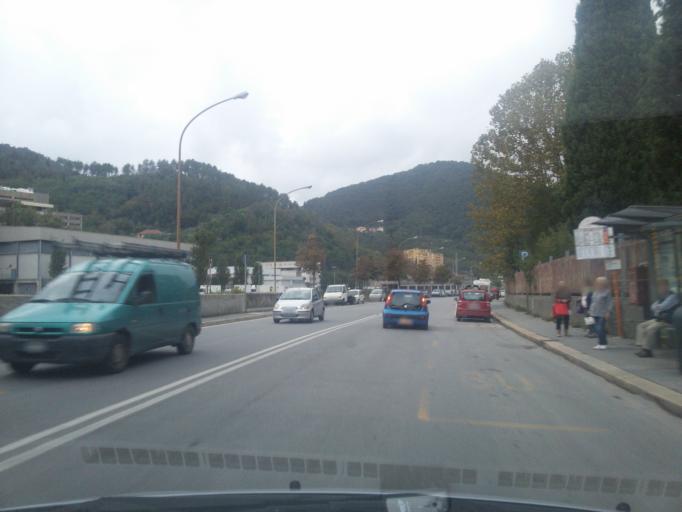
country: IT
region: Liguria
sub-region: Provincia di Genova
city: Piccarello
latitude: 44.4475
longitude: 9.0035
